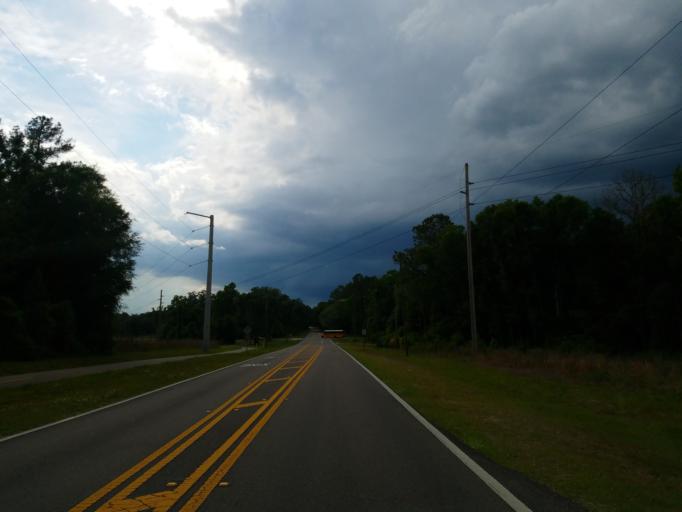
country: US
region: Florida
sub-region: Hernando County
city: Brooksville
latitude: 28.5554
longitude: -82.3611
